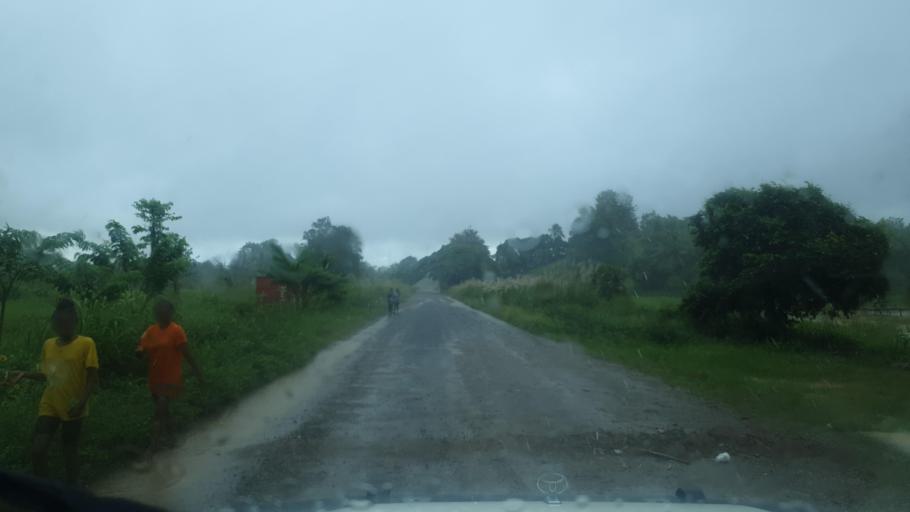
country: PG
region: Gulf
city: Kerema
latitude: -8.3864
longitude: 146.3621
